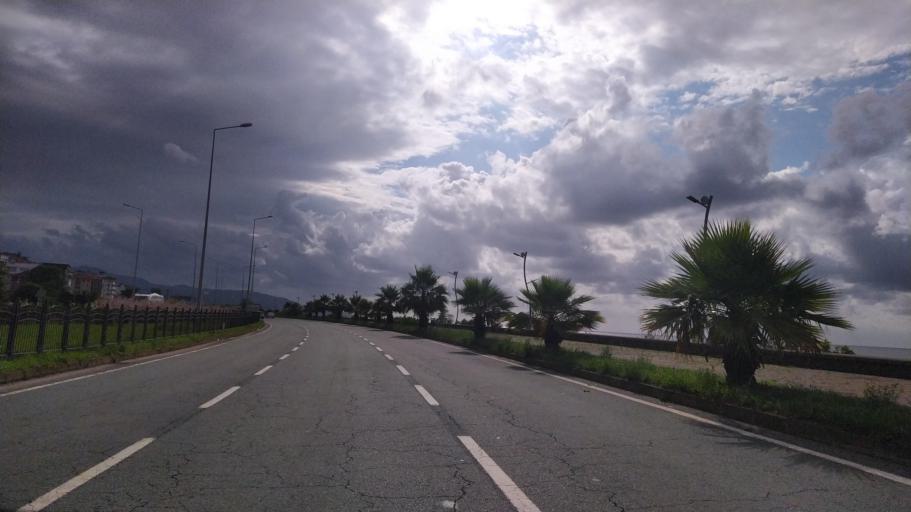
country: TR
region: Rize
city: Ardesen
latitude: 41.1947
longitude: 40.9816
